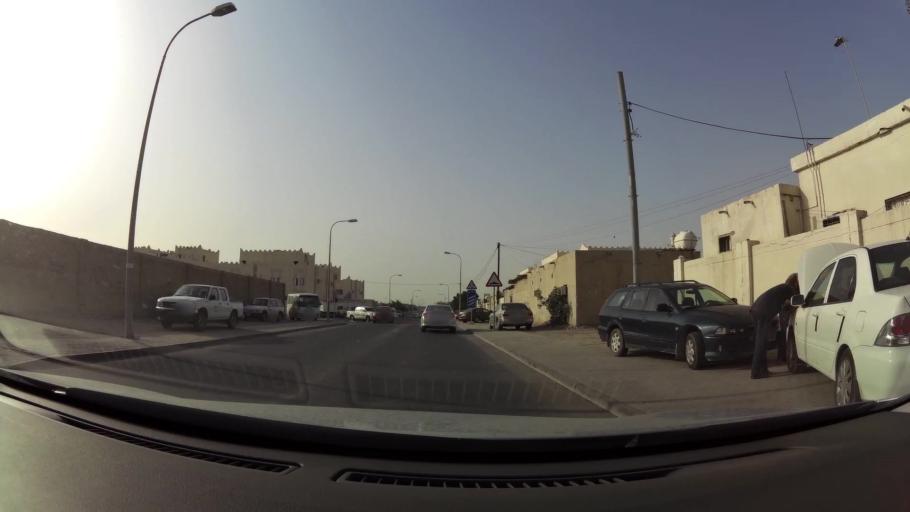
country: QA
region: Baladiyat ar Rayyan
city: Ar Rayyan
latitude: 25.2379
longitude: 51.4423
